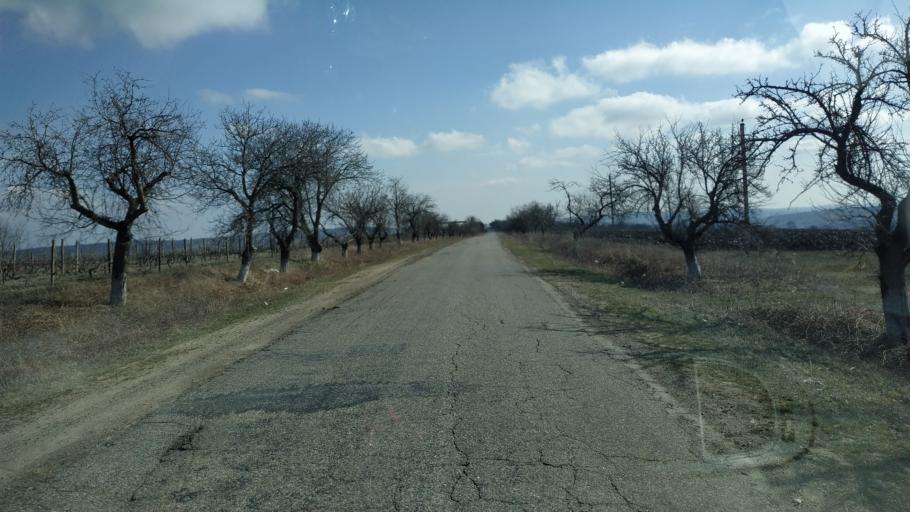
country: MD
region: Hincesti
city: Hincesti
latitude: 46.8502
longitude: 28.6494
